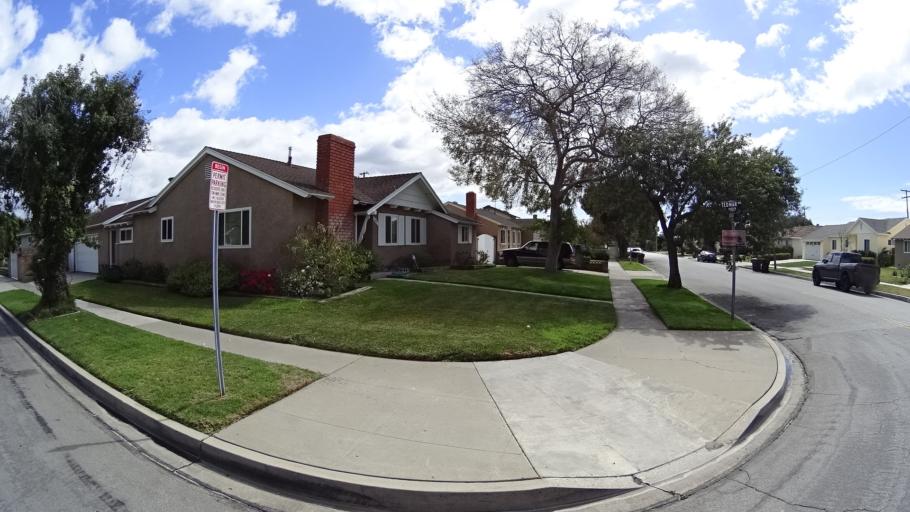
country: US
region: California
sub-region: Orange County
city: Anaheim
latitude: 33.8267
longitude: -117.9388
